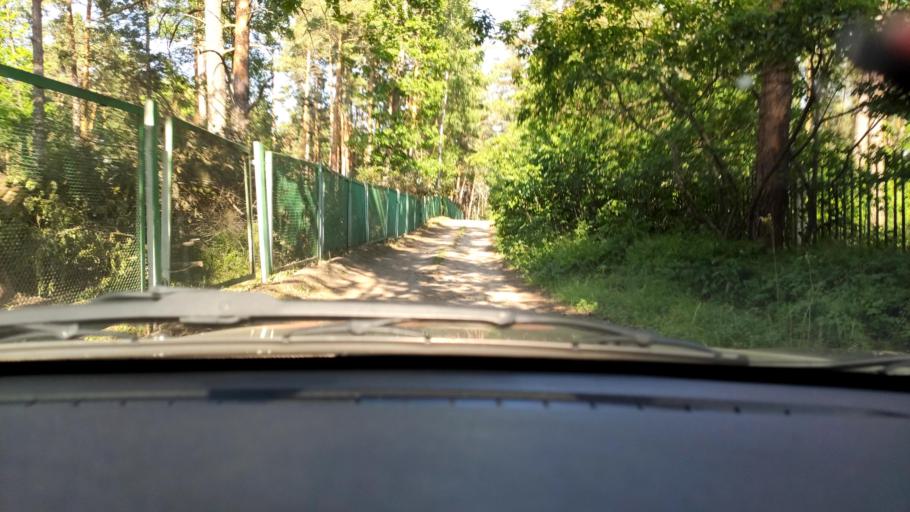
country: RU
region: Voronezj
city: Somovo
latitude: 51.7567
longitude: 39.3730
